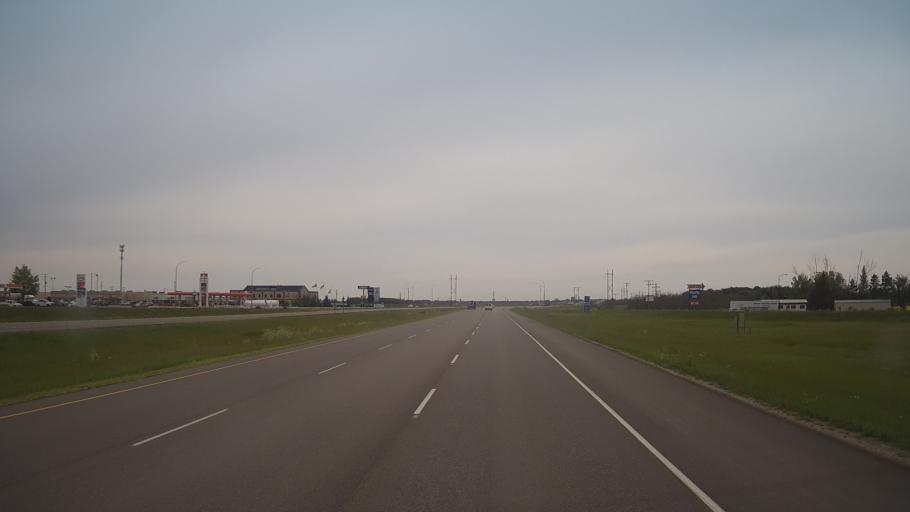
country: CA
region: Saskatchewan
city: Saskatoon
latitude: 52.0548
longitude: -106.5978
